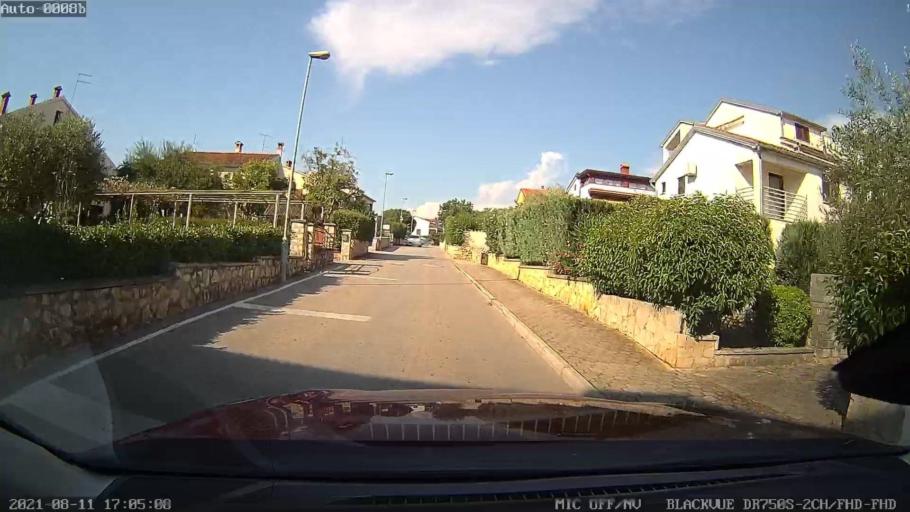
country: HR
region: Istarska
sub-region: Grad Rovinj
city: Rovinj
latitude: 45.0812
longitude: 13.6640
